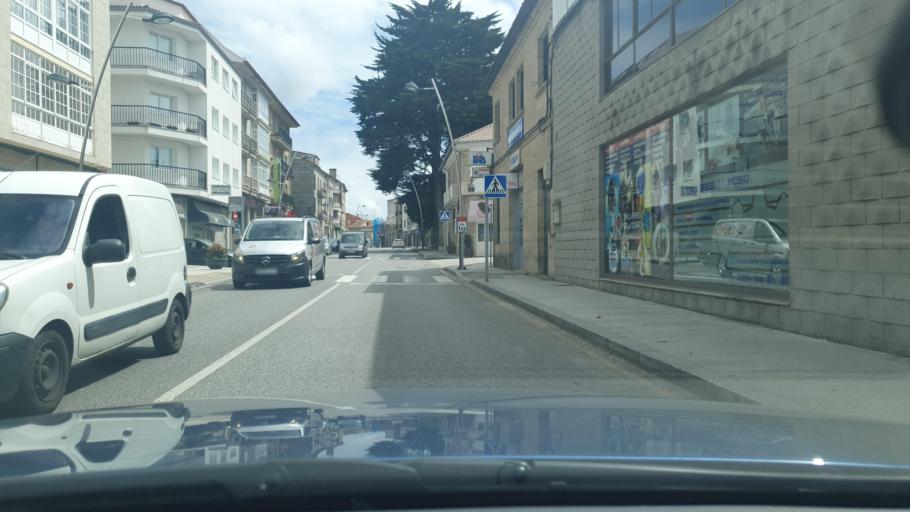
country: ES
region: Galicia
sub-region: Provincia de Pontevedra
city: Cambados
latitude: 42.5125
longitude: -8.8160
